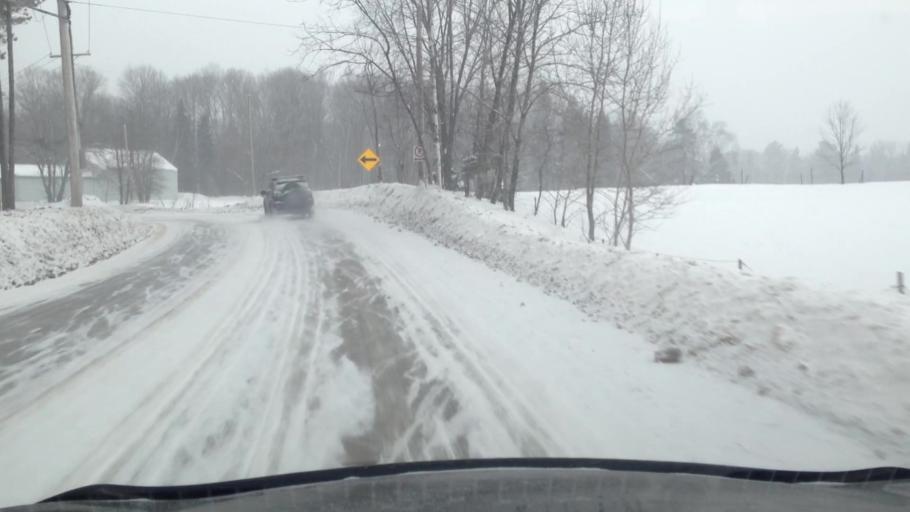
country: CA
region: Quebec
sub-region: Laurentides
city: Mont-Tremblant
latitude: 45.9716
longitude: -74.6286
